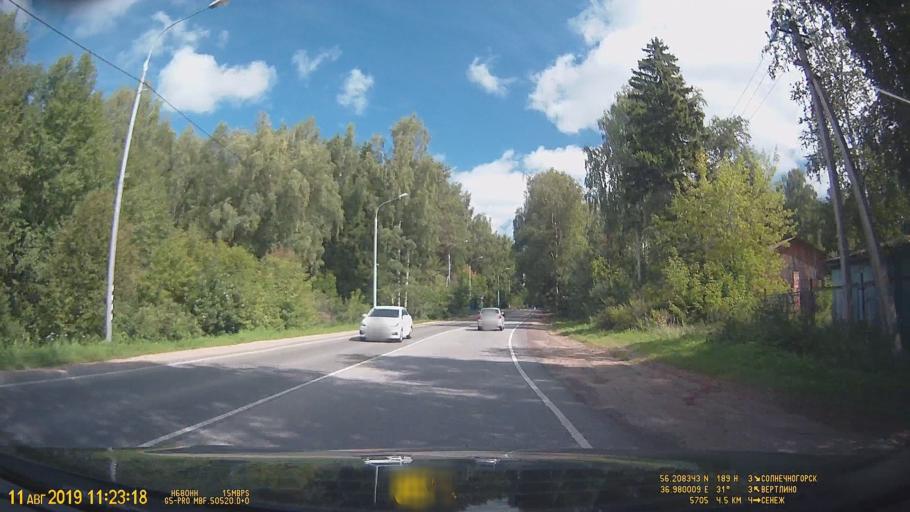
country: RU
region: Moskovskaya
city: Solnechnogorsk
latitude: 56.2085
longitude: 36.9802
